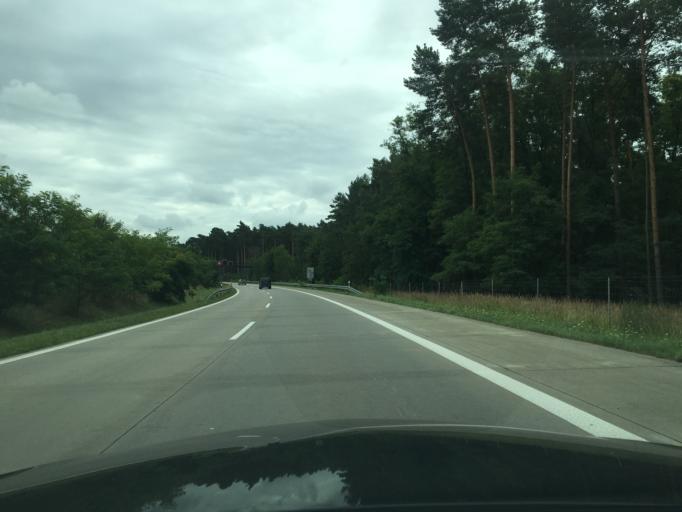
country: DE
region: Brandenburg
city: Borkwalde
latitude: 52.3303
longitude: 12.8186
